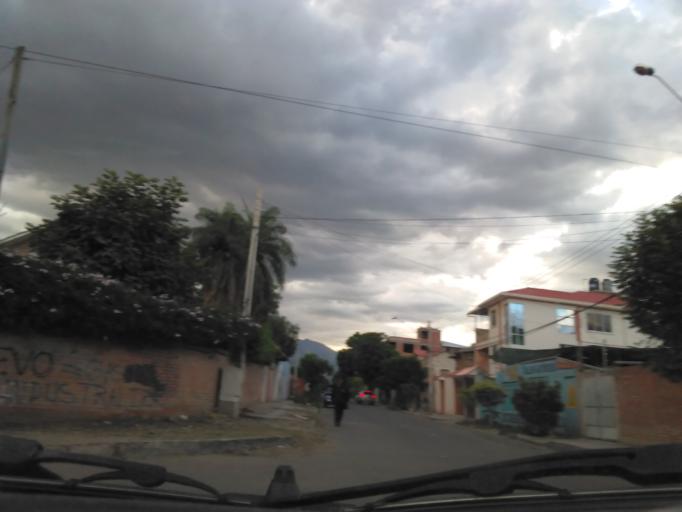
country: BO
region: Cochabamba
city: Cochabamba
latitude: -17.3610
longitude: -66.1728
